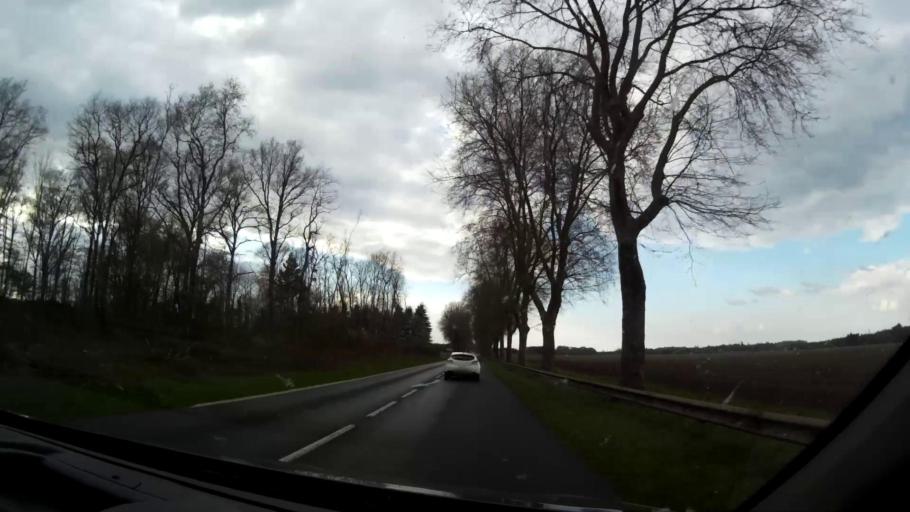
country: FR
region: Centre
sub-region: Departement du Loir-et-Cher
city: Cormeray
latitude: 47.4726
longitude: 1.4224
